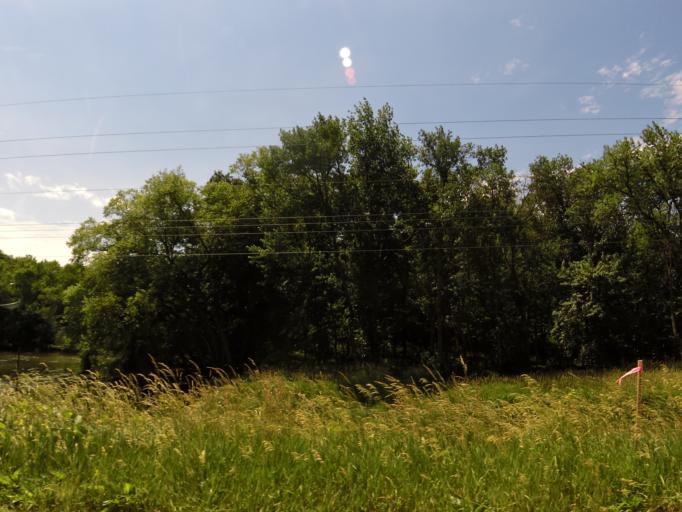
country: US
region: Iowa
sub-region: Bremer County
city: Tripoli
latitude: 42.7148
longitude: -92.1698
